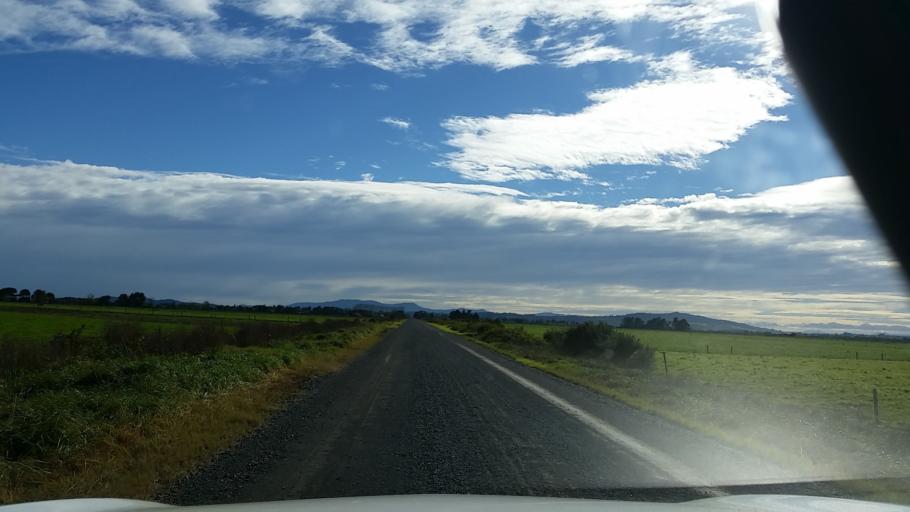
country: NZ
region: Waikato
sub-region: Hamilton City
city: Hamilton
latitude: -37.6812
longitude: 175.4437
